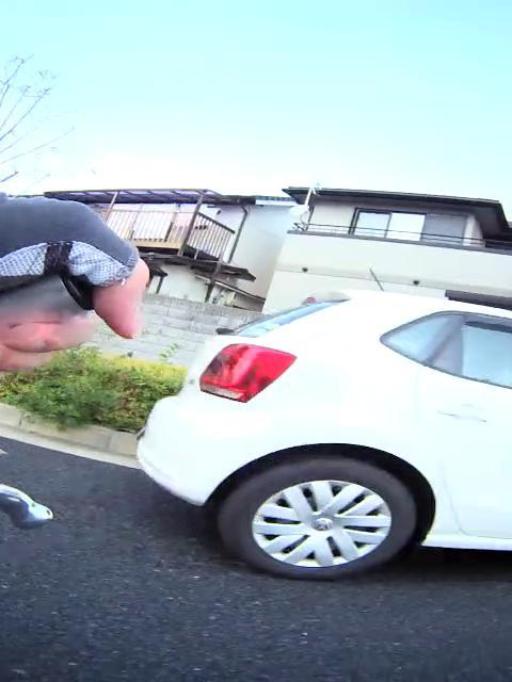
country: JP
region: Osaka
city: Suita
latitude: 34.7370
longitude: 135.5130
